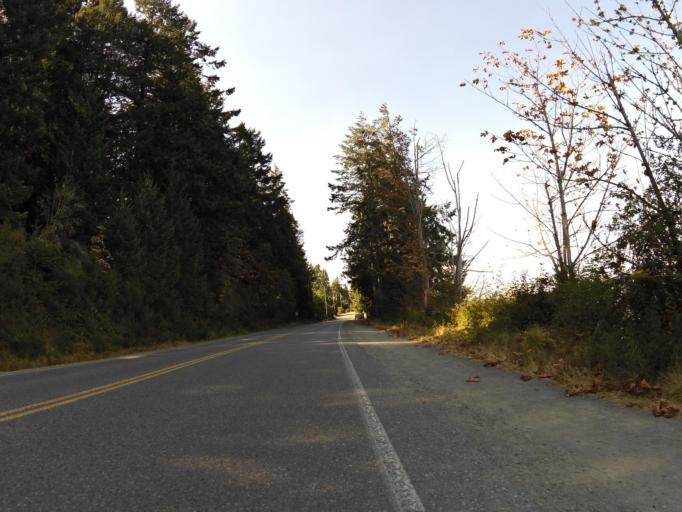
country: CA
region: British Columbia
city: North Saanich
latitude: 48.6358
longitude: -123.5359
